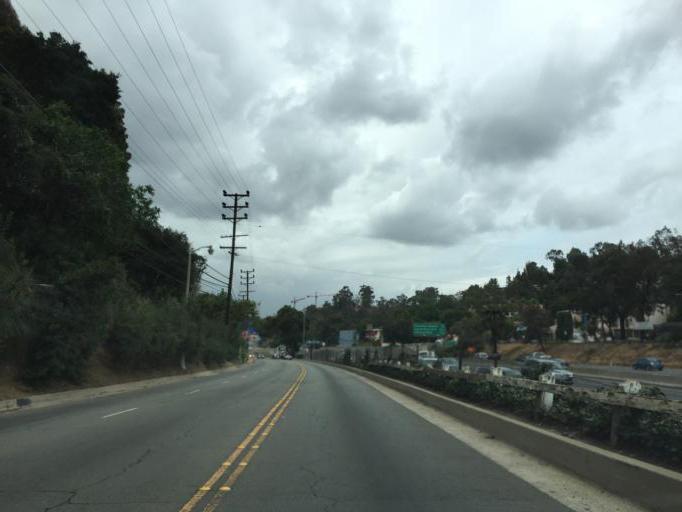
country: US
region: California
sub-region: Los Angeles County
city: Universal City
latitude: 34.1253
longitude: -118.3443
